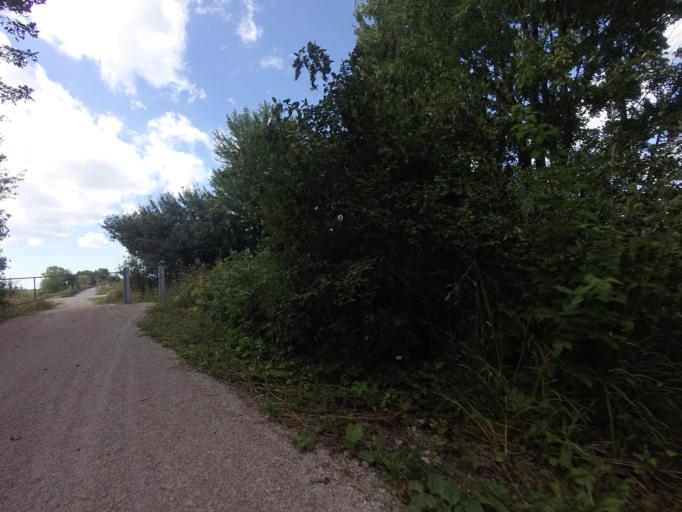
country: CA
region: Ontario
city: Huron East
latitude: 43.7163
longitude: -81.3873
